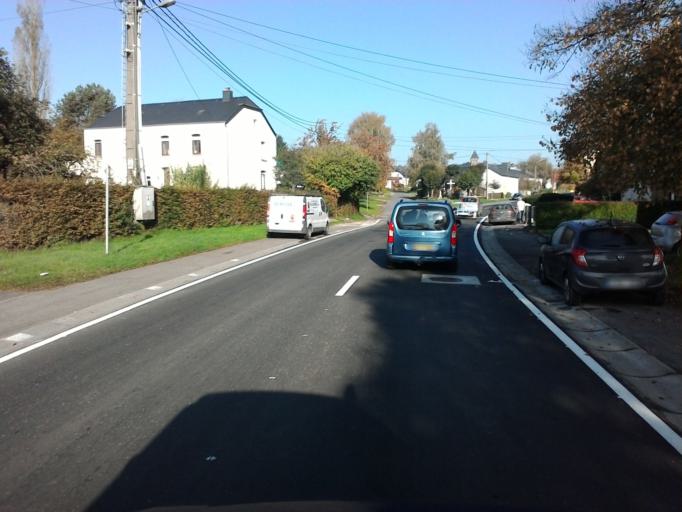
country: BE
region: Wallonia
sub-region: Province du Luxembourg
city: Florenville
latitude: 49.7126
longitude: 5.3203
